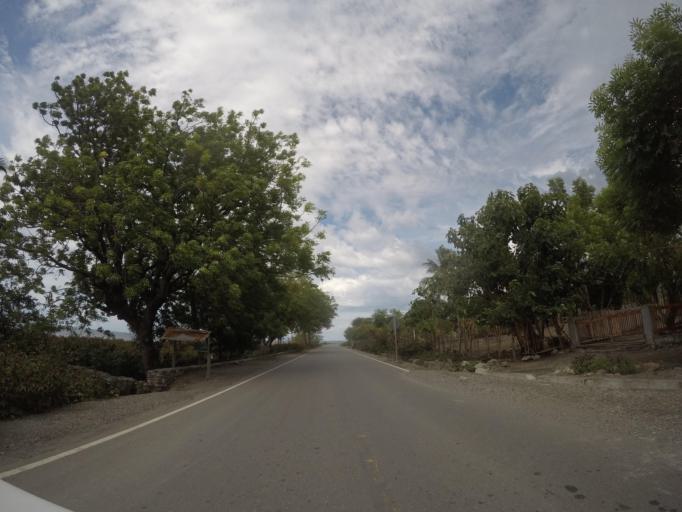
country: TL
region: Liquica
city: Maubara
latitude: -8.6086
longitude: 125.2068
